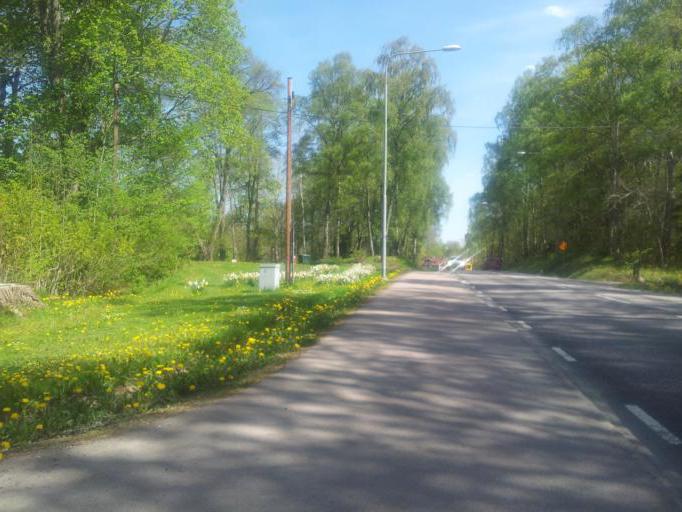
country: SE
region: Uppsala
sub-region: Knivsta Kommun
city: Knivsta
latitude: 59.8717
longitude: 17.9556
